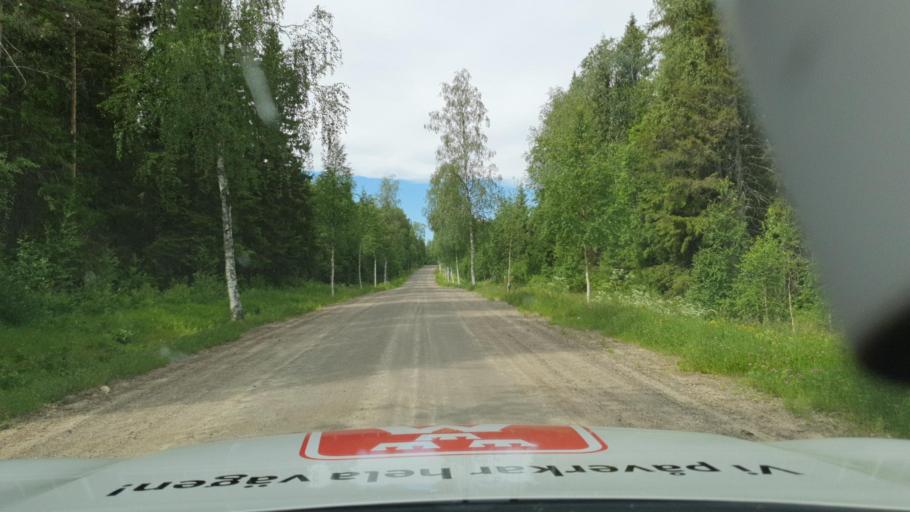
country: SE
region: Vaesterbotten
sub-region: Skelleftea Kommun
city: Burtraesk
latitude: 64.4720
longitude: 20.4518
